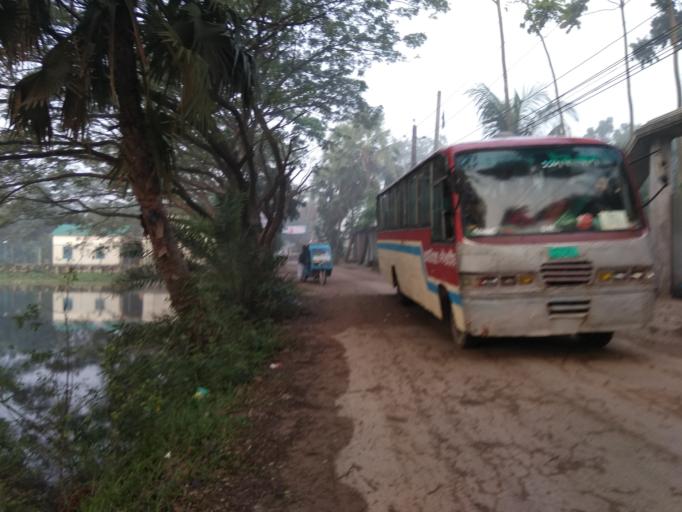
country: BD
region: Dhaka
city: Tungi
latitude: 23.8612
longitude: 90.4499
